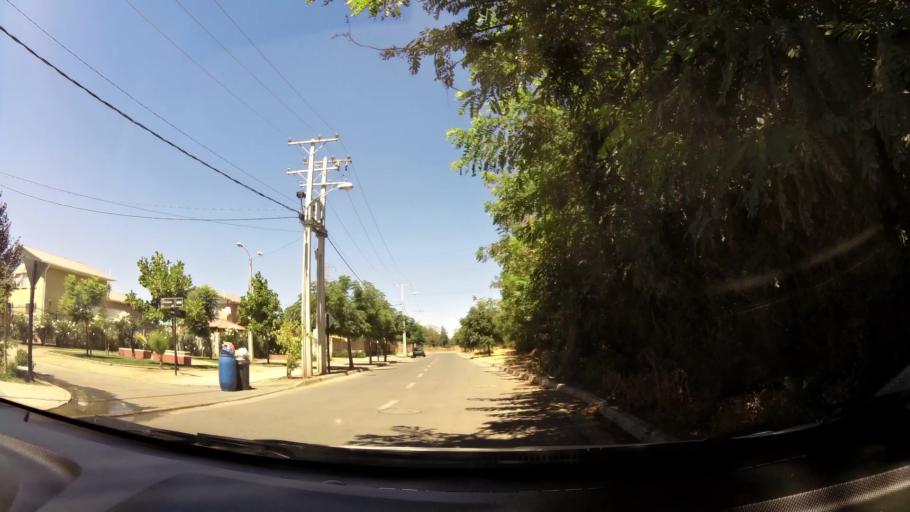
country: CL
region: O'Higgins
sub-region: Provincia de Cachapoal
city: Rancagua
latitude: -34.1427
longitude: -70.7260
